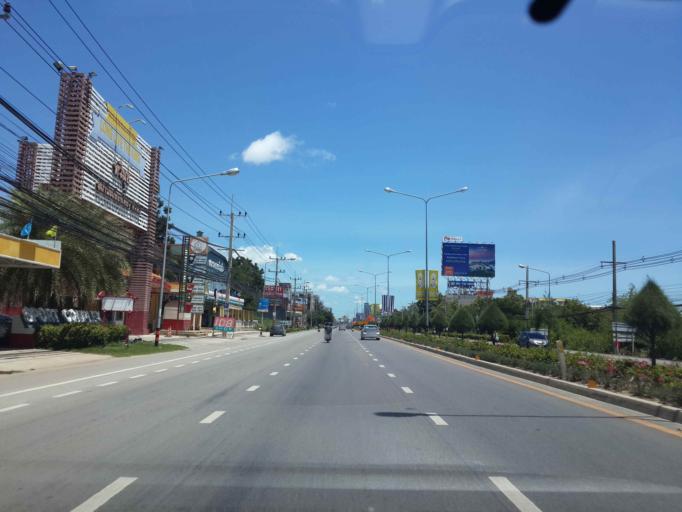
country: TH
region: Prachuap Khiri Khan
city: Hua Hin
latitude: 12.6111
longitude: 99.9502
